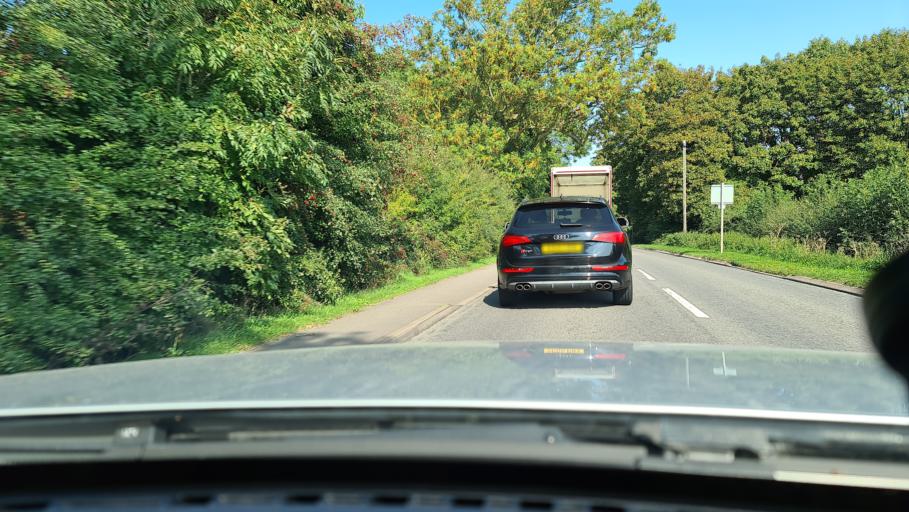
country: GB
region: England
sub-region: Northamptonshire
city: Daventry
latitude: 52.3296
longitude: -1.1762
